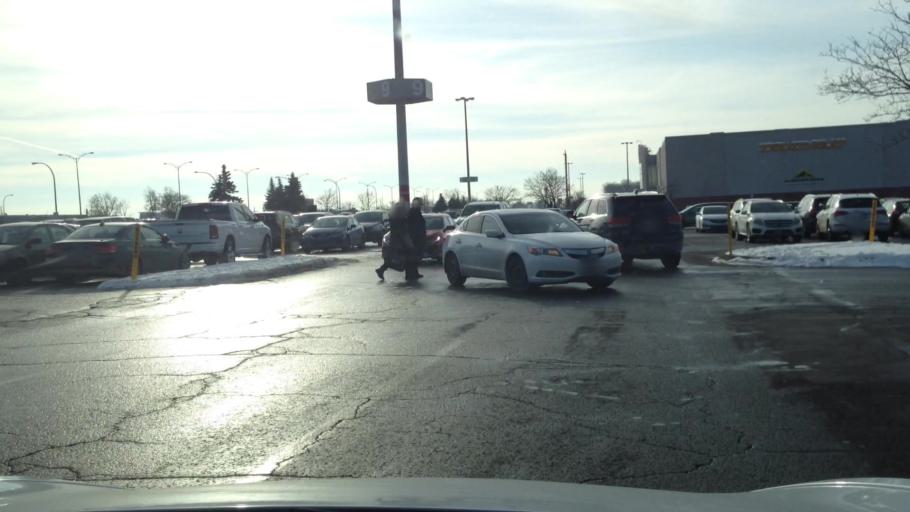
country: CA
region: Quebec
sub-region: Montreal
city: Pointe-Claire
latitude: 45.4640
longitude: -73.8282
